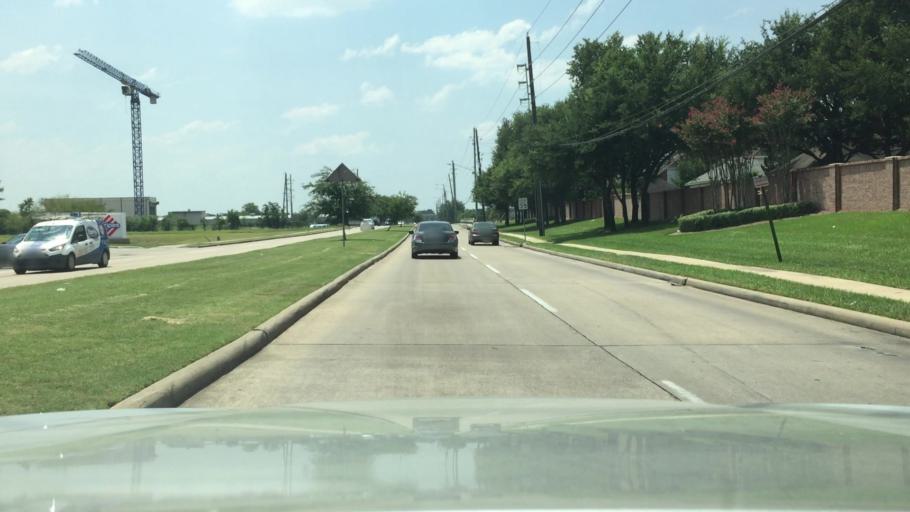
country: US
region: Texas
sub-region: Fort Bend County
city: Meadows Place
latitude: 29.7243
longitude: -95.5925
